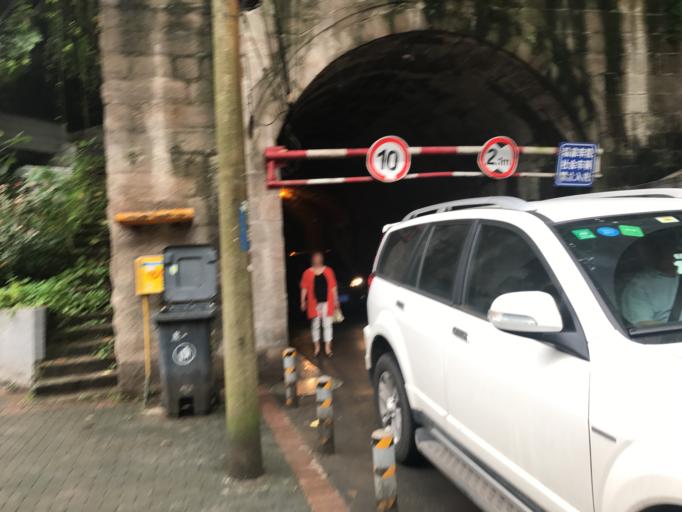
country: CN
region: Chongqing Shi
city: Nanping
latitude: 29.5644
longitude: 106.5949
